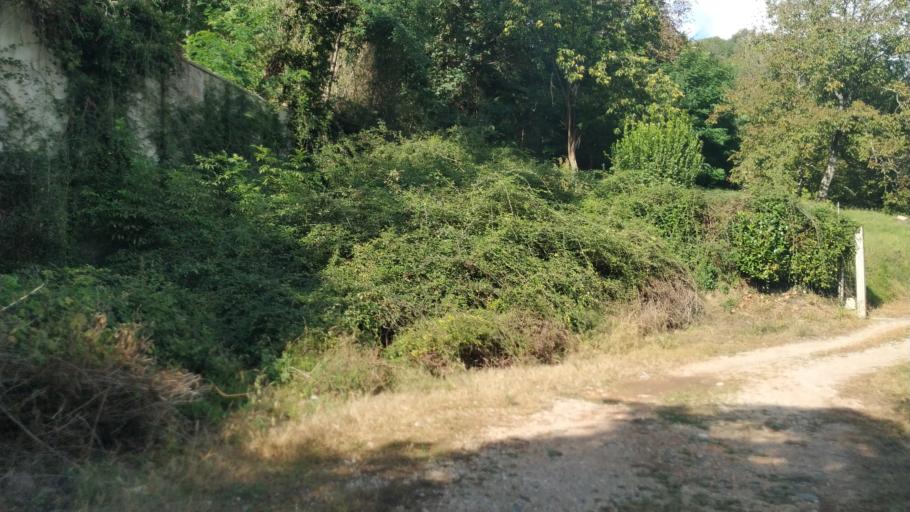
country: IT
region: Piedmont
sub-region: Provincia di Novara
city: Grignasco
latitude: 45.6873
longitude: 8.3354
